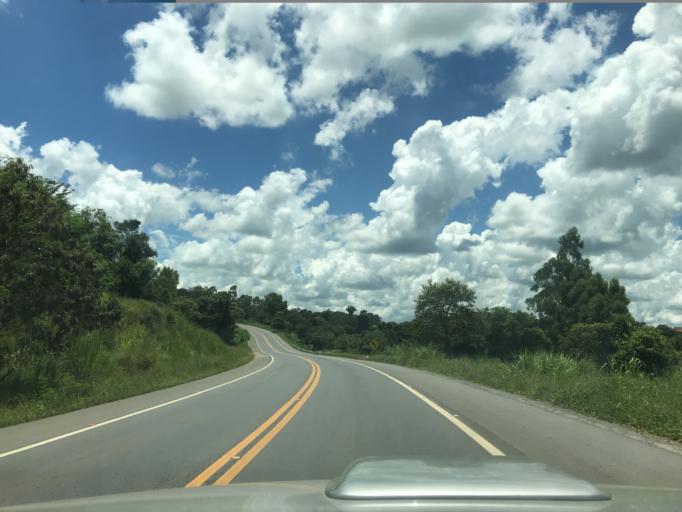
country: BR
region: Minas Gerais
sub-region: Perdoes
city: Perdoes
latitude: -21.0902
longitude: -45.0985
